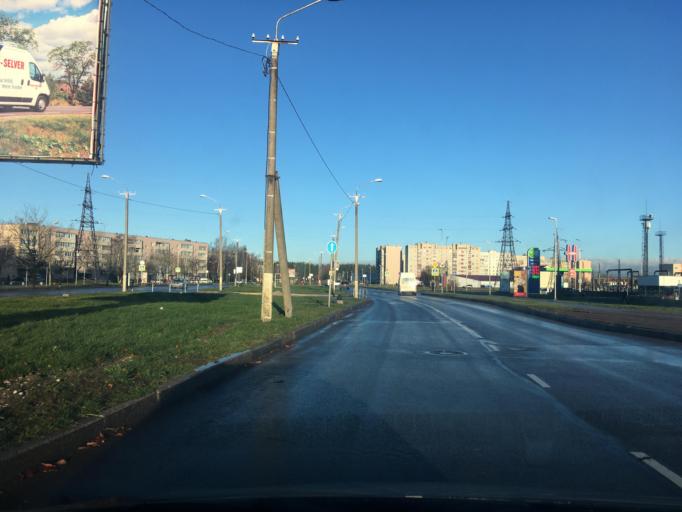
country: EE
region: Ida-Virumaa
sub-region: Narva linn
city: Narva
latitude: 59.3862
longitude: 28.1764
